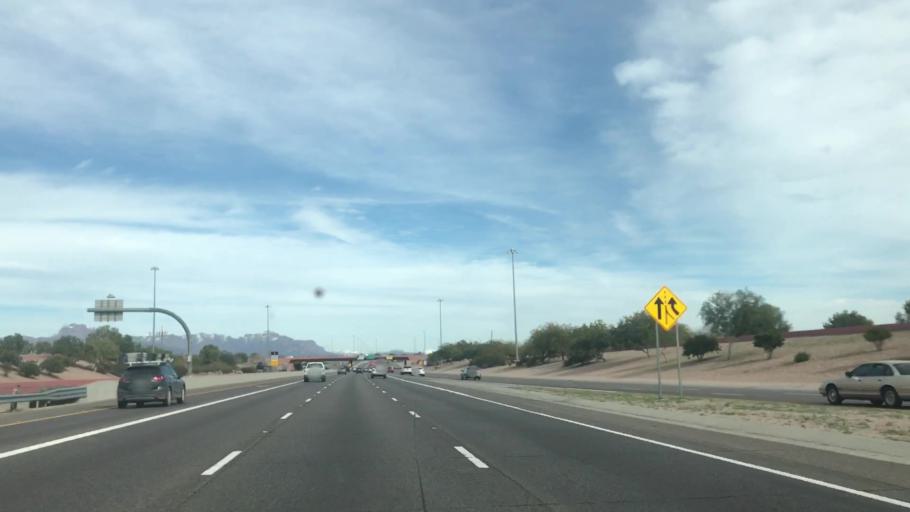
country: US
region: Arizona
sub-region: Pinal County
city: Apache Junction
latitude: 33.3863
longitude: -111.6386
